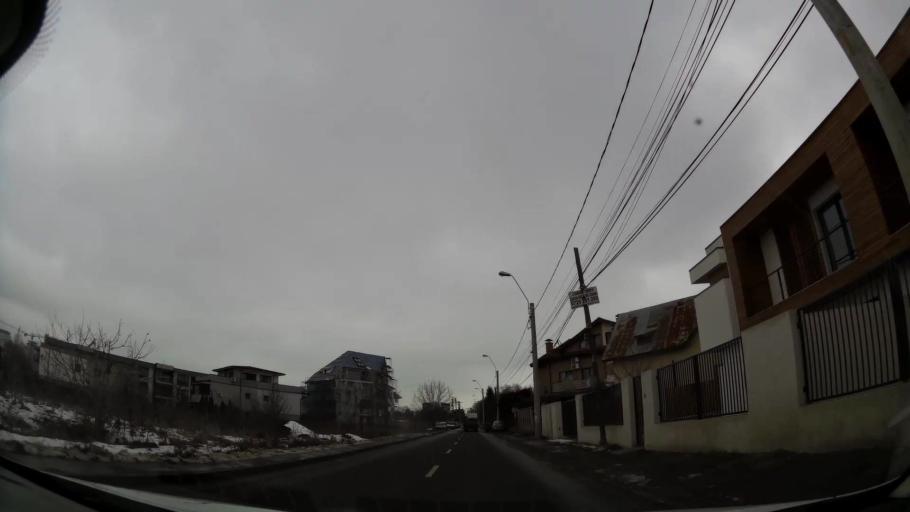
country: RO
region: Ilfov
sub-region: Comuna Otopeni
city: Otopeni
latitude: 44.5045
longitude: 26.0507
